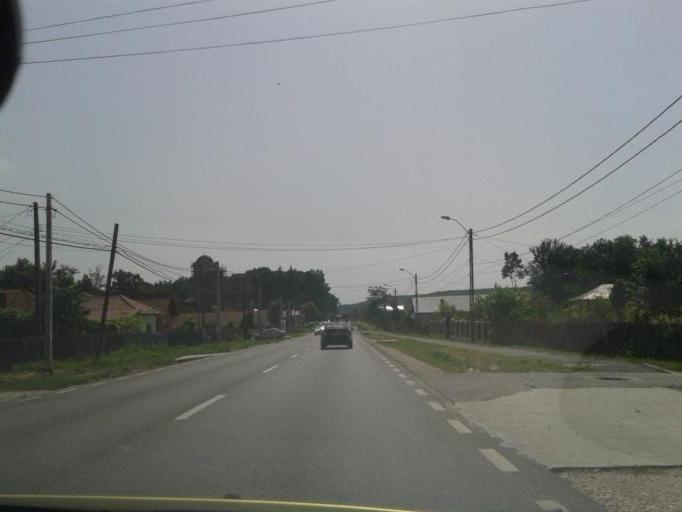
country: RO
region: Arges
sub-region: Comuna Bascov
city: Bascov
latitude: 44.8884
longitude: 24.7718
